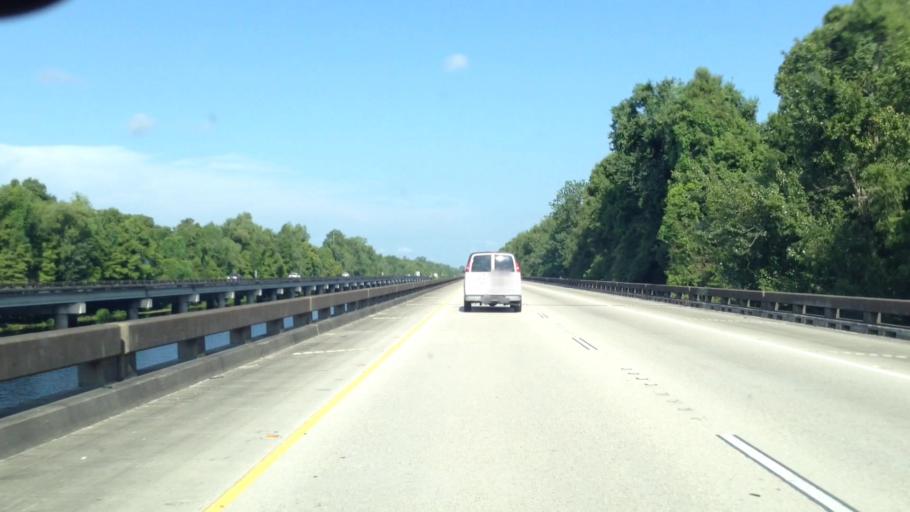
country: US
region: Louisiana
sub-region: Saint John the Baptist Parish
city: Reserve
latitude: 30.1122
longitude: -90.5556
